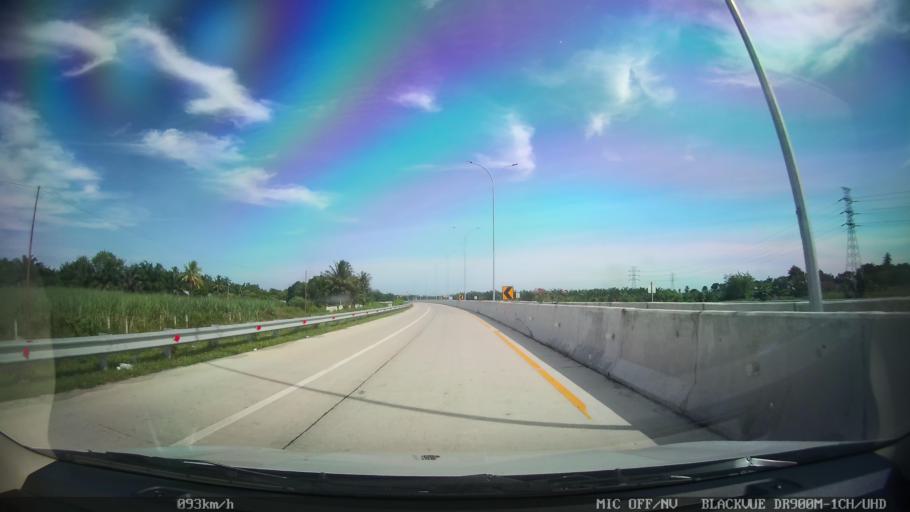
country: ID
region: North Sumatra
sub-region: Kabupaten Langkat
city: Stabat
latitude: 3.7268
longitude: 98.4919
